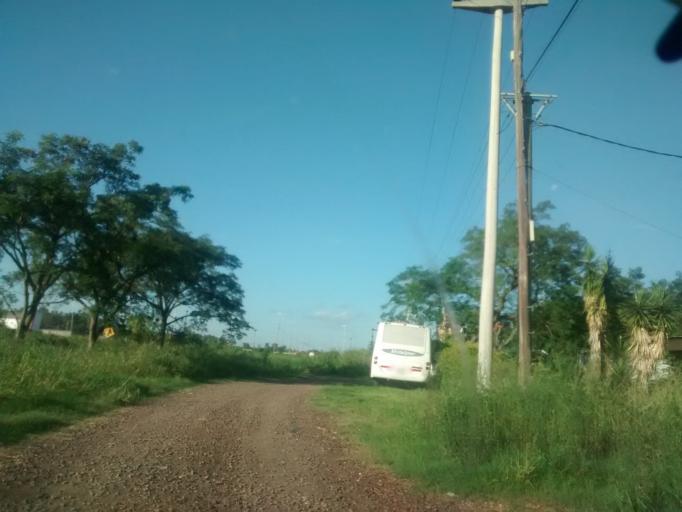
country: AR
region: Chaco
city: Fontana
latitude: -27.4532
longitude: -59.0306
